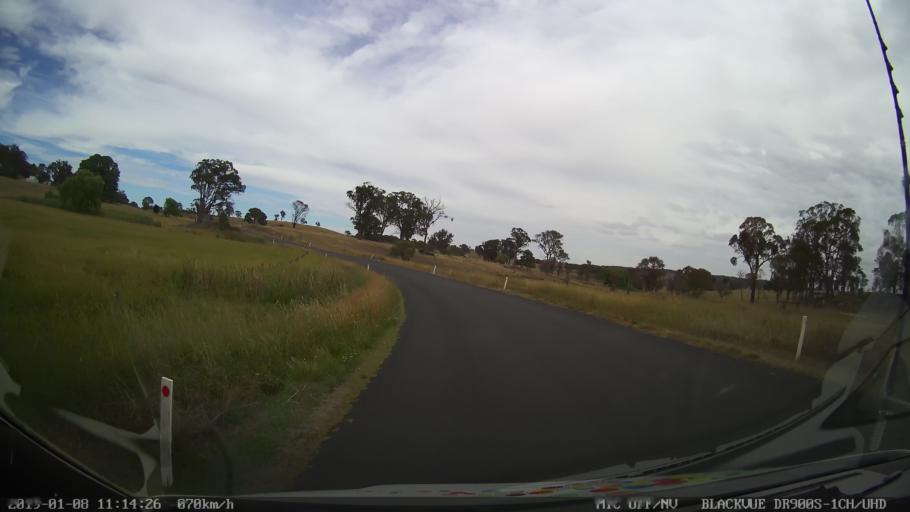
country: AU
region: New South Wales
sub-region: Guyra
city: Guyra
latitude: -30.2258
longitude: 151.5894
